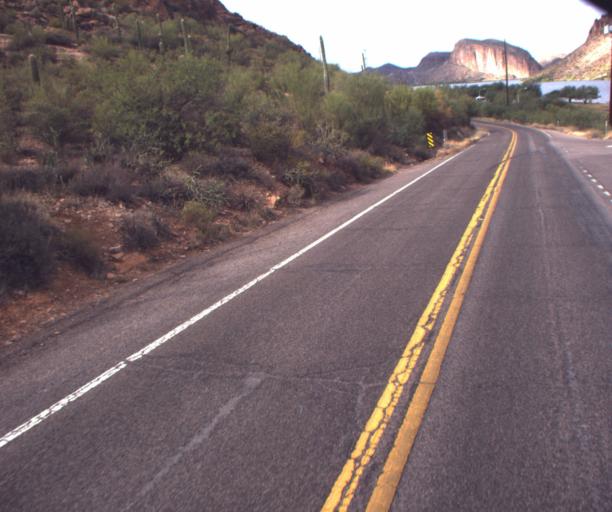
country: US
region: Arizona
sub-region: Pinal County
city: Apache Junction
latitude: 33.5331
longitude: -111.4175
